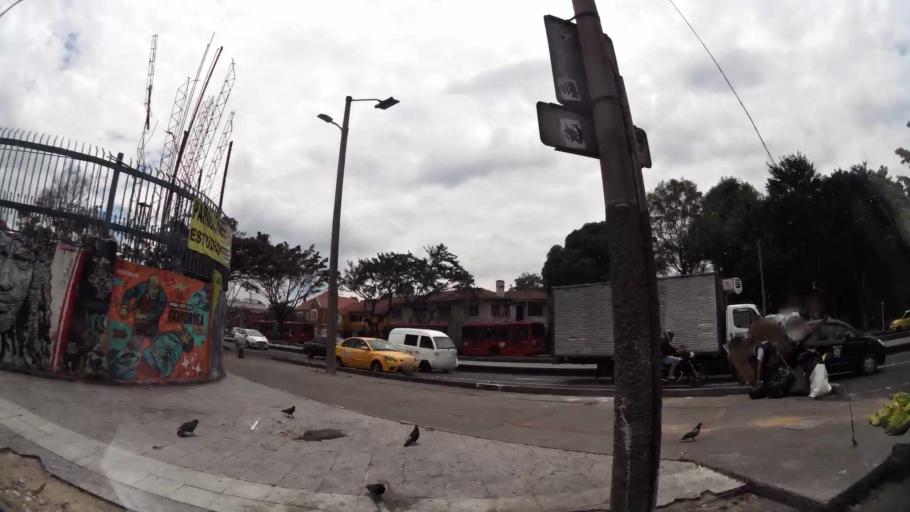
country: CO
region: Bogota D.C.
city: Bogota
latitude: 4.6289
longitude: -74.0682
